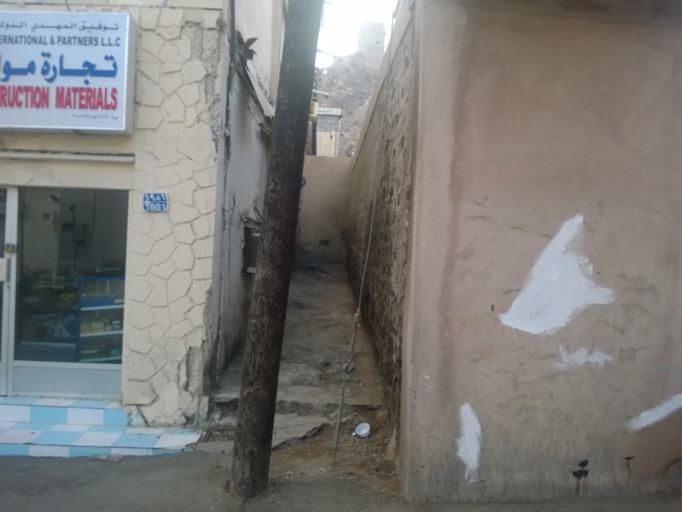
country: OM
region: Muhafazat Masqat
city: Muscat
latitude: 23.6170
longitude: 58.5641
